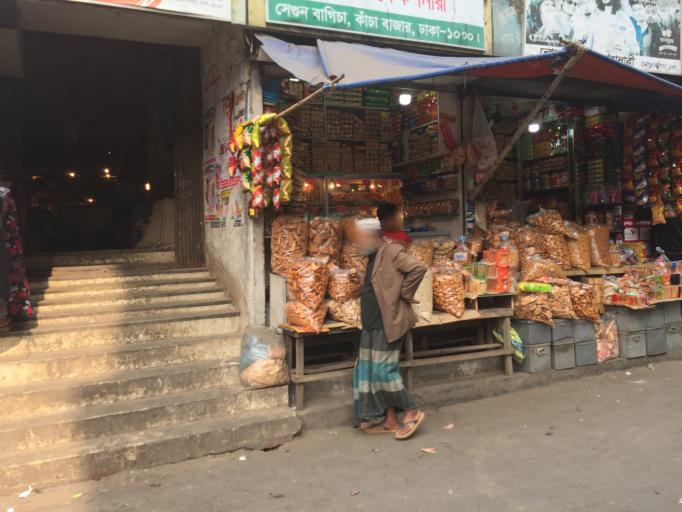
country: BD
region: Dhaka
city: Paltan
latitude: 23.7335
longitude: 90.4091
